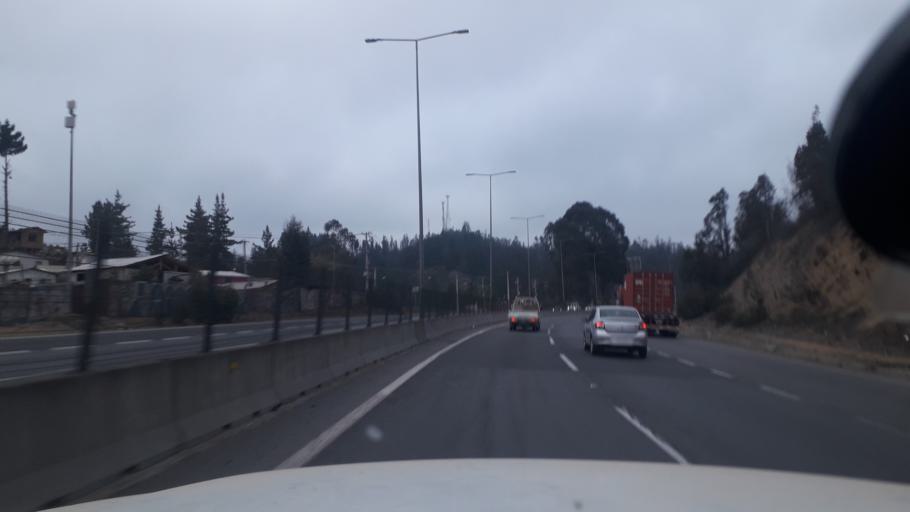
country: CL
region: Valparaiso
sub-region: Provincia de Valparaiso
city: Vina del Mar
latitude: -33.1112
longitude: -71.5596
